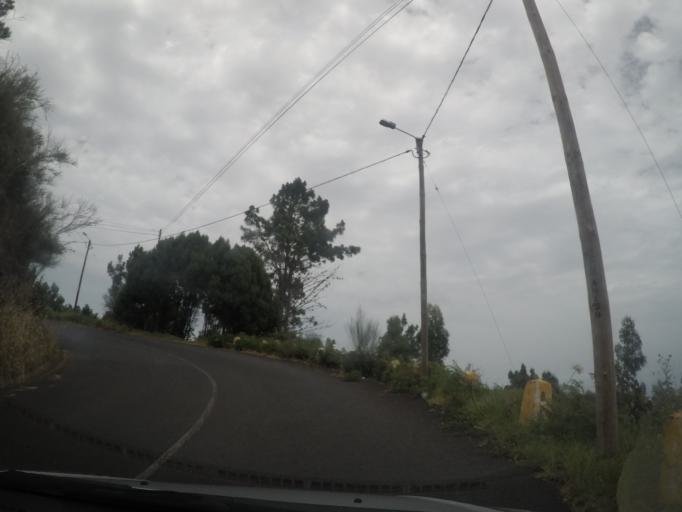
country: PT
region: Madeira
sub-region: Santa Cruz
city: Camacha
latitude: 32.6873
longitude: -16.8292
